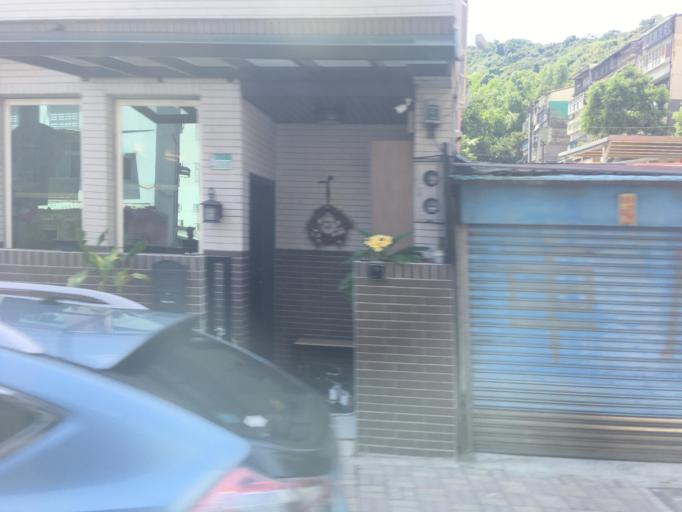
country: TW
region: Taipei
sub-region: Taipei
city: Banqiao
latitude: 25.0475
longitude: 121.4268
